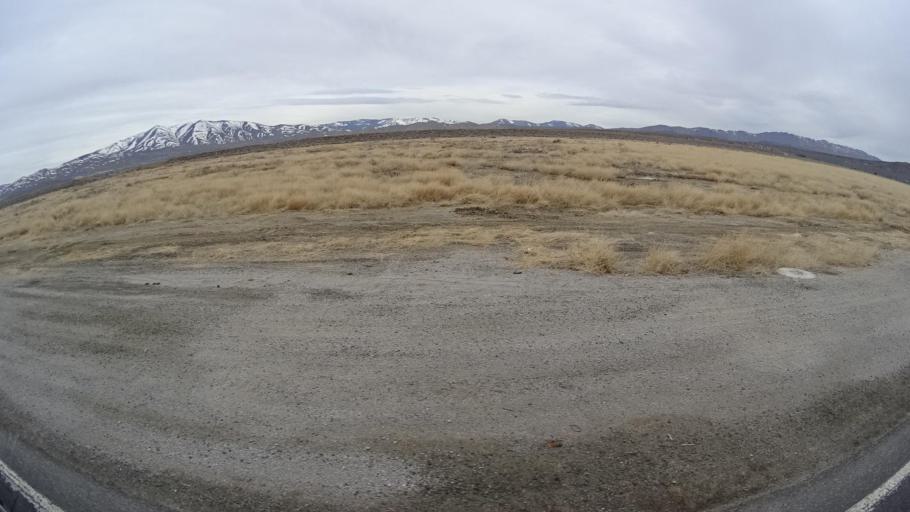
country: US
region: Nevada
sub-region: Washoe County
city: Lemmon Valley
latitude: 39.6605
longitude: -119.8283
